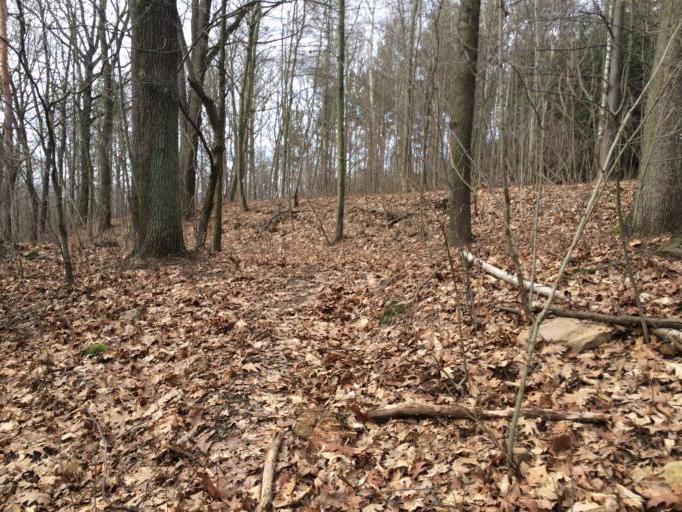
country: PL
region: Lower Silesian Voivodeship
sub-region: Powiat lwowecki
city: Lwowek Slaski
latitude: 51.1081
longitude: 15.6214
